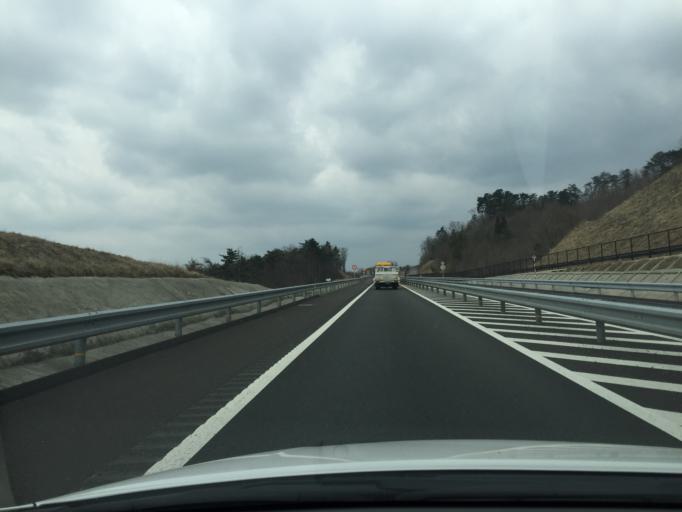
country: JP
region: Miyagi
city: Marumori
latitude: 37.8387
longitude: 140.8791
